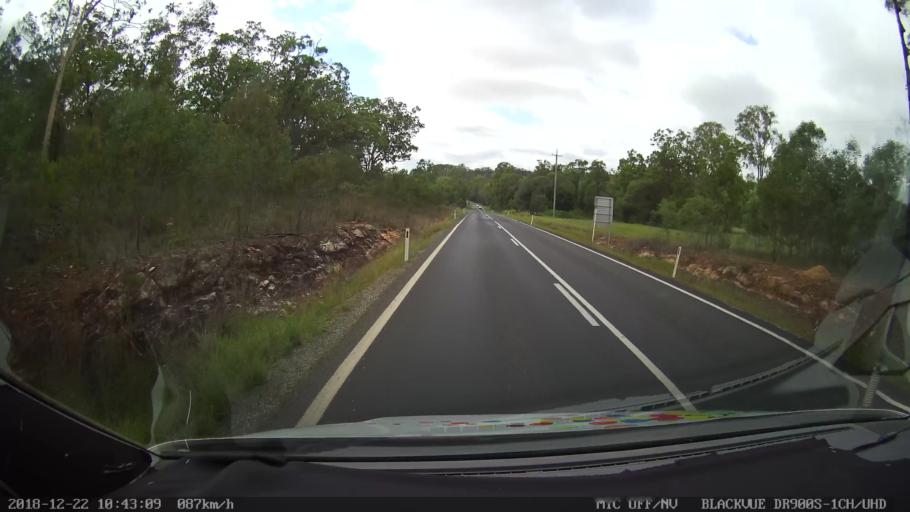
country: AU
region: New South Wales
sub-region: Clarence Valley
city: South Grafton
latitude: -29.6427
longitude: 152.7851
